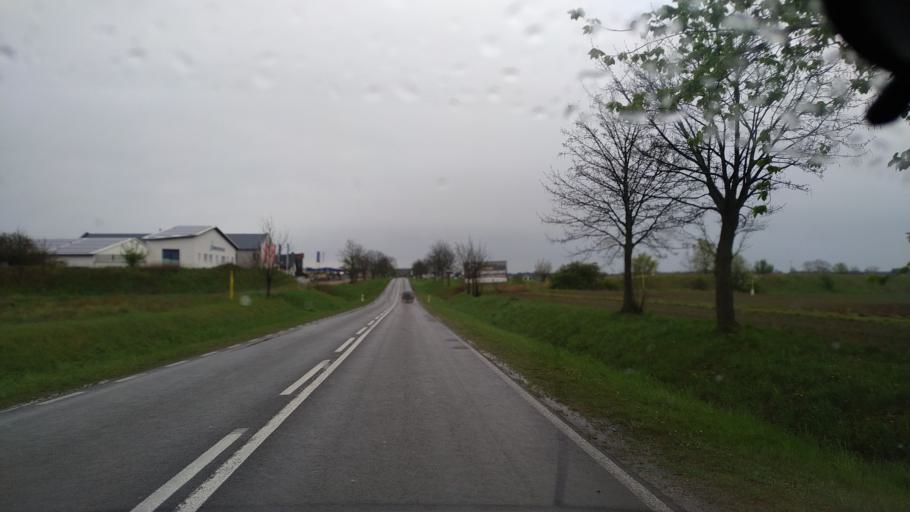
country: PL
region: Greater Poland Voivodeship
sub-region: Powiat zlotowski
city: Zlotow
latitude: 53.3373
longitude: 17.0130
